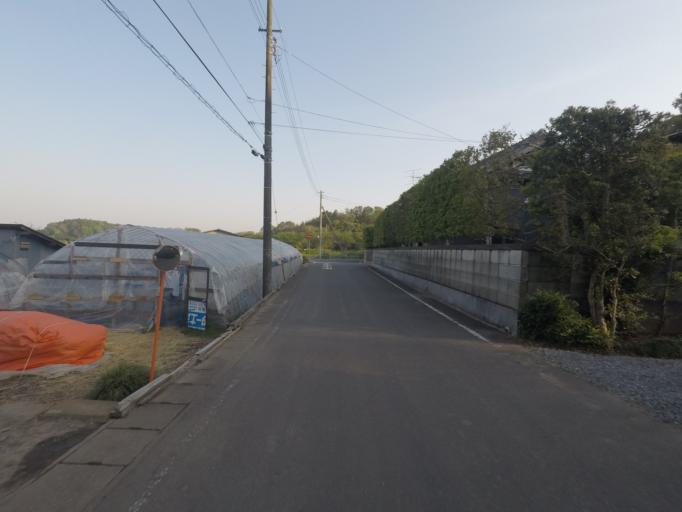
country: JP
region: Ibaraki
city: Naka
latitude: 36.0960
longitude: 140.1318
